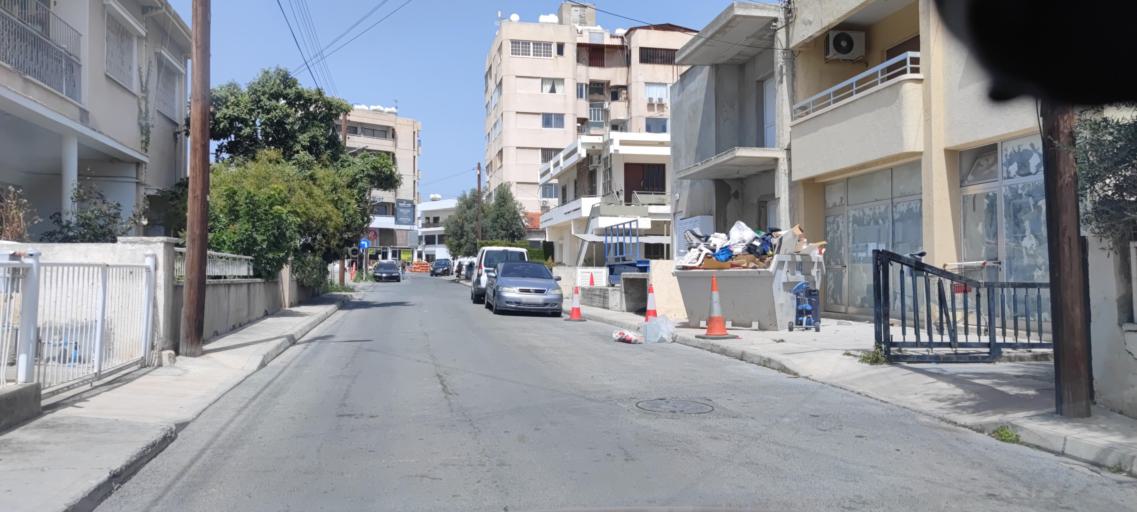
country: CY
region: Limassol
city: Limassol
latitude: 34.6772
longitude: 33.0238
